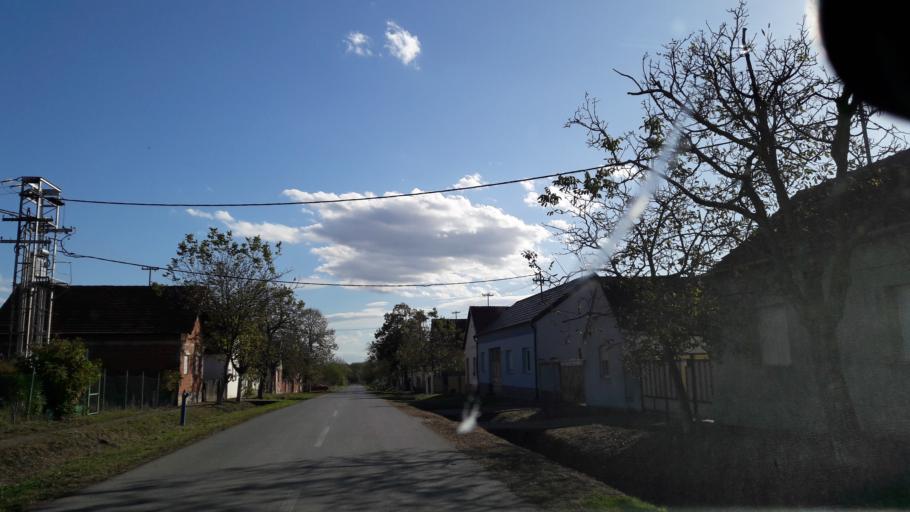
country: HR
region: Osjecko-Baranjska
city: Vukojevci
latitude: 45.3966
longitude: 18.2397
